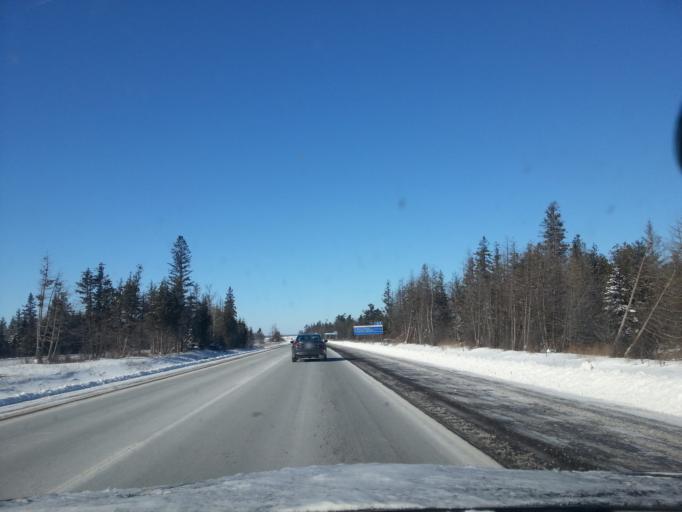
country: CA
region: Ontario
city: Arnprior
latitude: 45.3520
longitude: -76.2111
